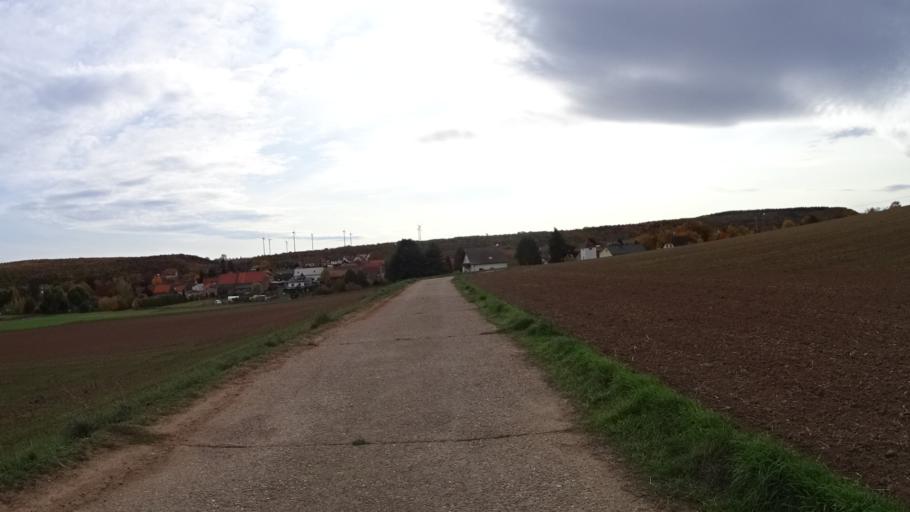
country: DE
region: Rheinland-Pfalz
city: Wendelsheim
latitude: 49.7684
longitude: 7.9897
